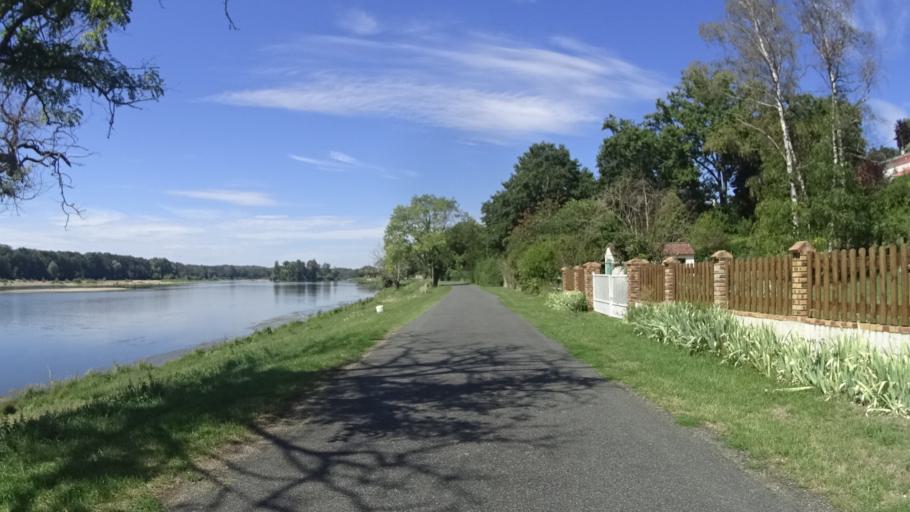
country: FR
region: Centre
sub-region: Departement du Loiret
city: Bonny-sur-Loire
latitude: 47.5858
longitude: 2.7945
